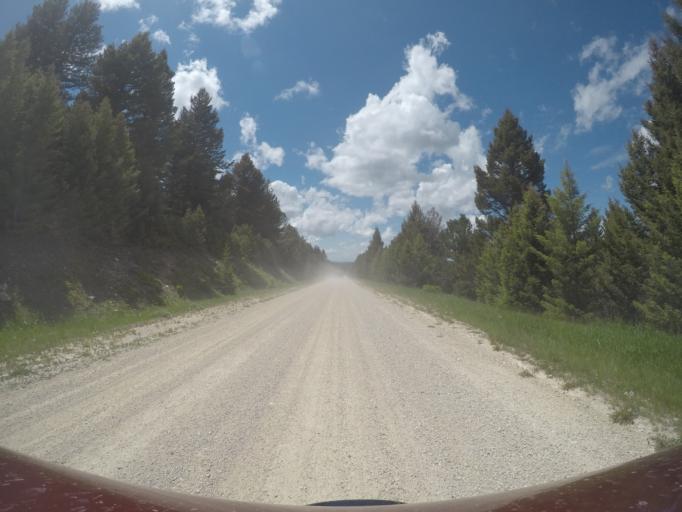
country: US
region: Wyoming
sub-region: Big Horn County
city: Lovell
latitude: 45.2040
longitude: -108.5223
